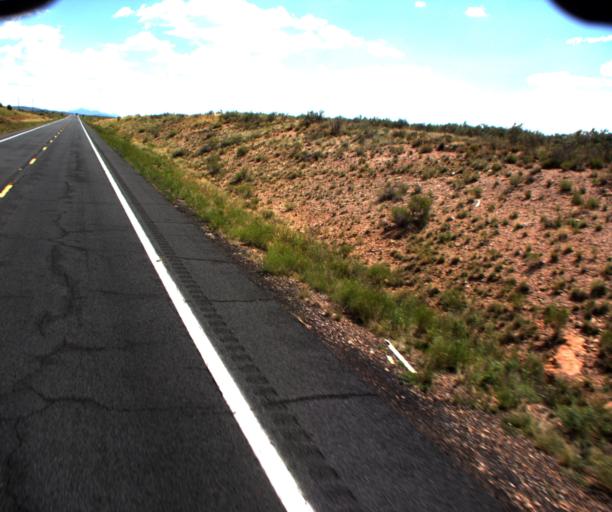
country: US
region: Arizona
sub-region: Coconino County
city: Williams
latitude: 35.6325
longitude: -112.1422
